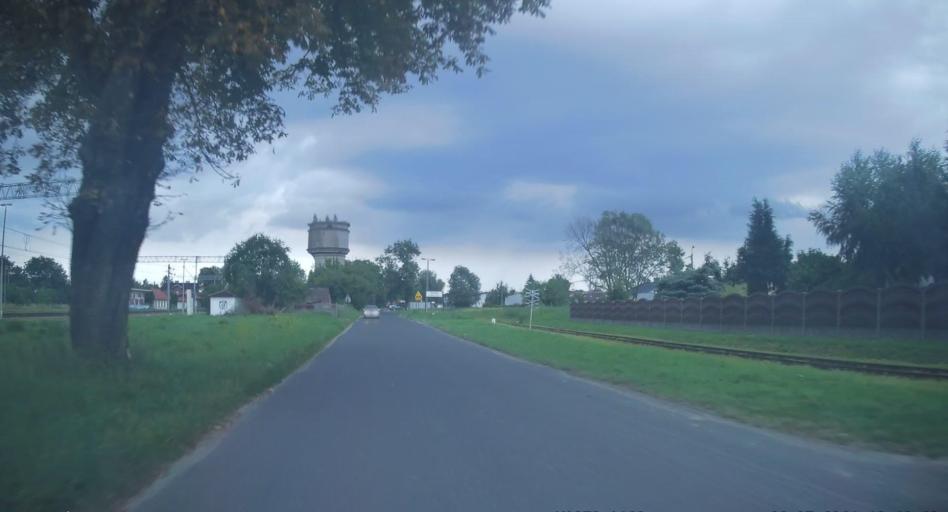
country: PL
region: Lodz Voivodeship
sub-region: Powiat brzezinski
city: Rogow
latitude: 51.8158
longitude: 19.8836
